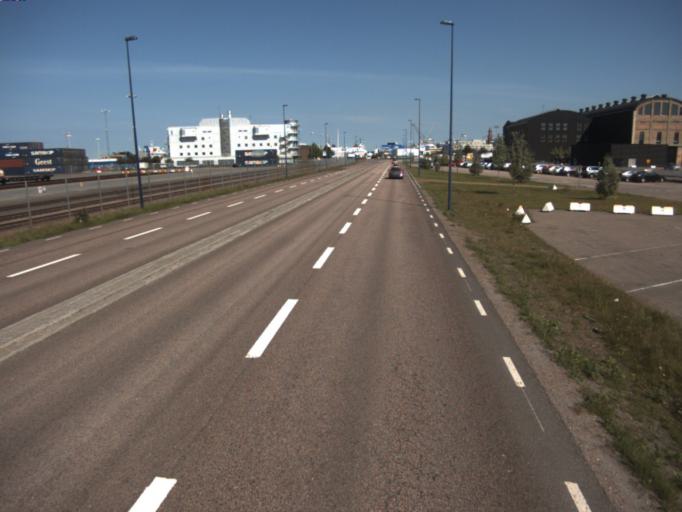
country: SE
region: Skane
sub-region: Helsingborg
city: Helsingborg
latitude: 56.0366
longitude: 12.6968
